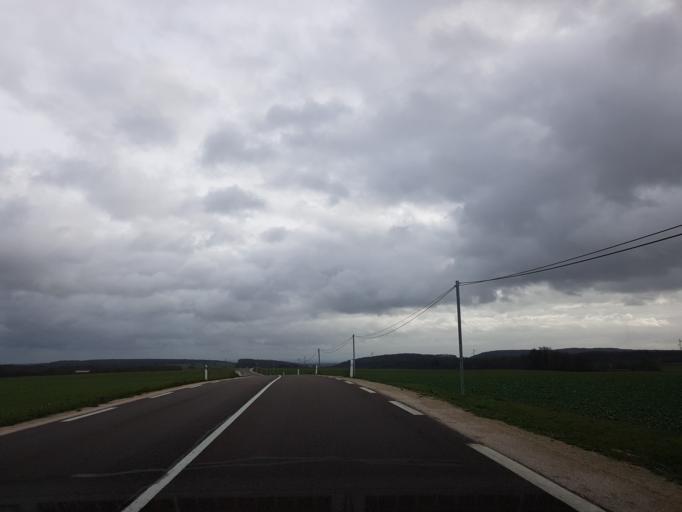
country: FR
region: Champagne-Ardenne
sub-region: Departement de la Haute-Marne
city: Fayl-Billot
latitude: 47.7639
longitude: 5.7113
